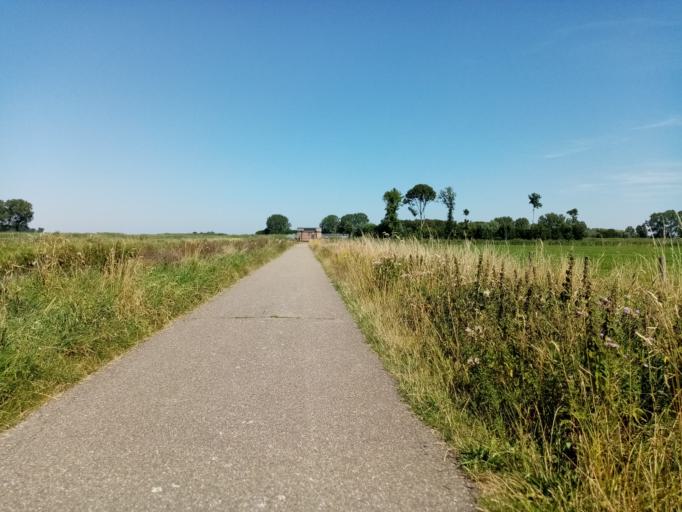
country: NL
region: North Brabant
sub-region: Gemeente Breda
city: Hoge Vucht
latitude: 51.6408
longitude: 4.7358
